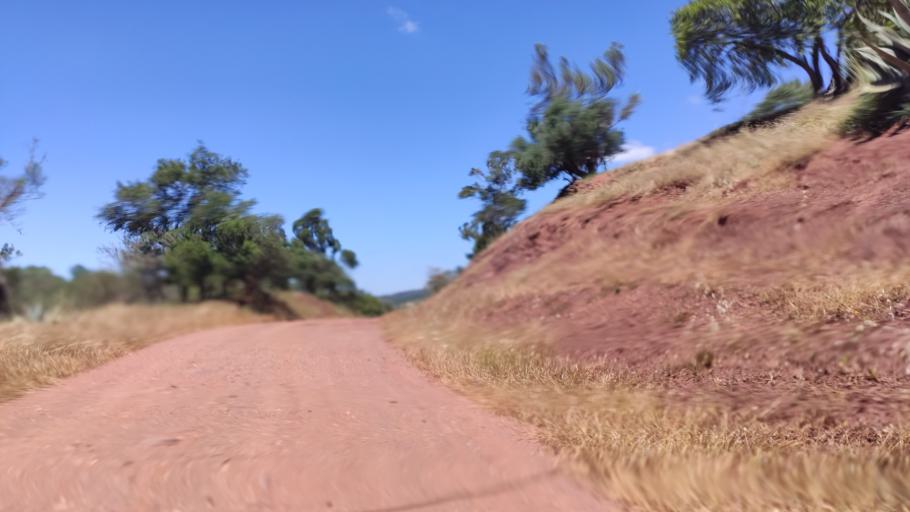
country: PT
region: Faro
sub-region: Sao Bras de Alportel
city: Sao Bras de Alportel
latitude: 37.1745
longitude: -7.9285
